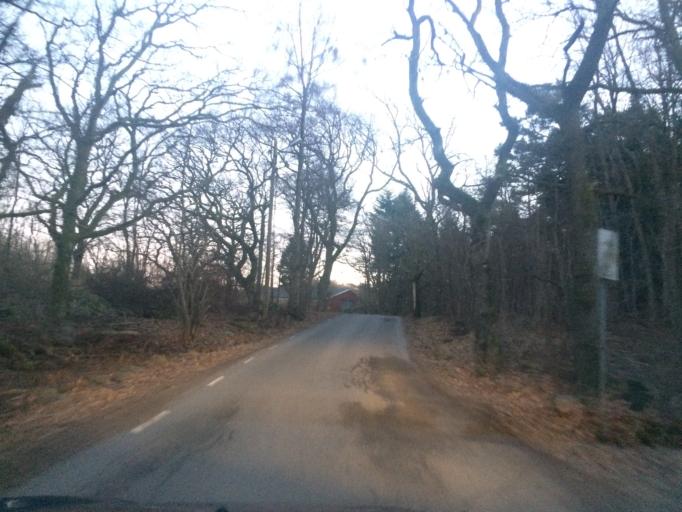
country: SE
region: Vaestra Goetaland
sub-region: Goteborg
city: Torslanda
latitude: 57.7887
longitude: 11.8335
